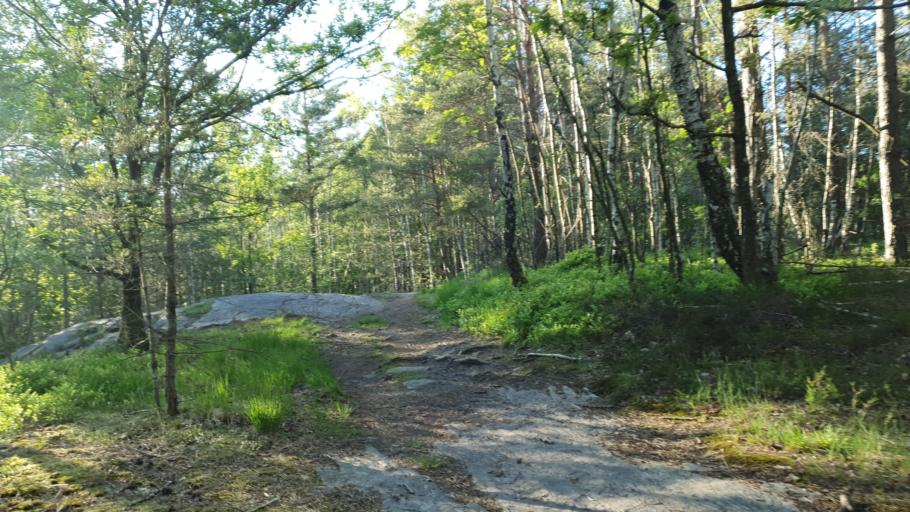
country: SE
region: Vaestra Goetaland
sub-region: Molndal
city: Kallered
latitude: 57.6360
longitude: 12.0547
